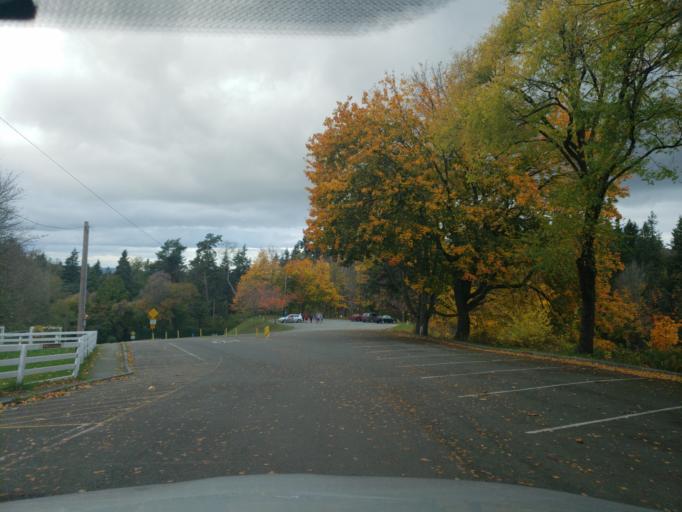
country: US
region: Washington
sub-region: Snohomish County
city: Everett
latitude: 47.9598
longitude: -122.2218
